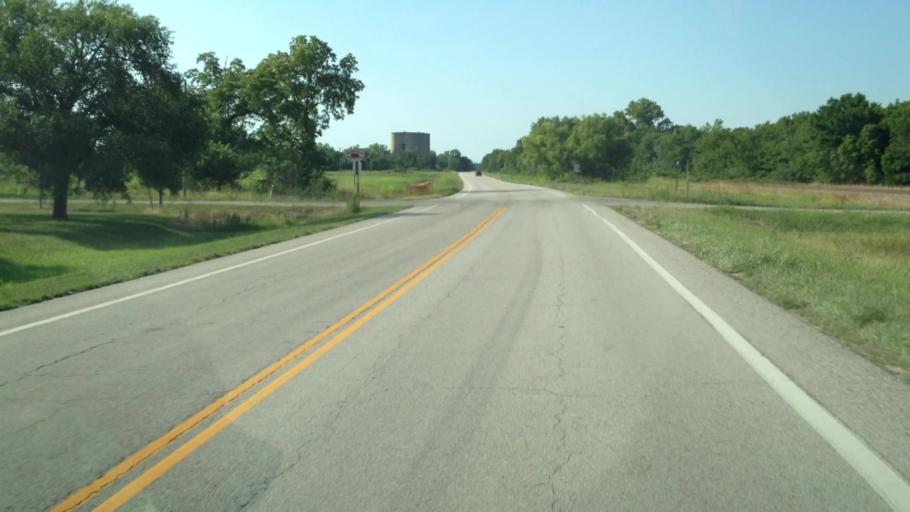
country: US
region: Kansas
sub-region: Allen County
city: Iola
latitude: 38.0228
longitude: -95.1710
